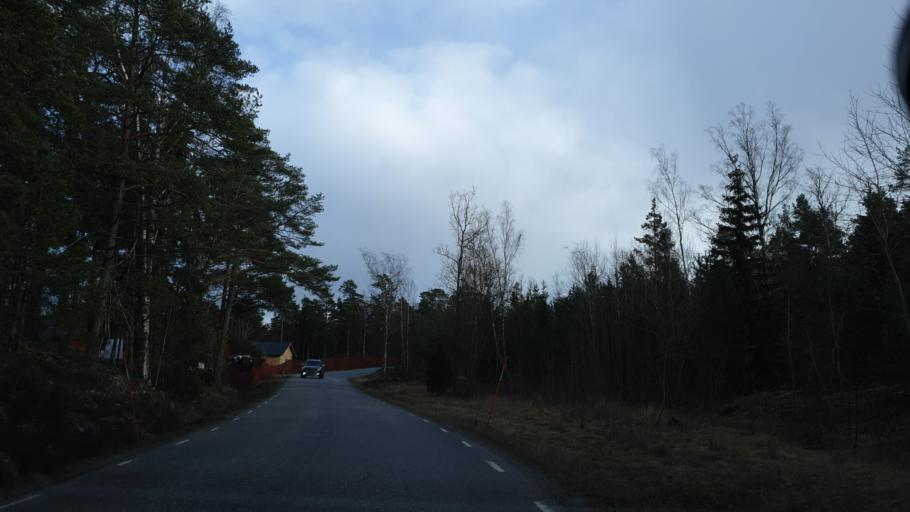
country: SE
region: Stockholm
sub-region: Varmdo Kommun
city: Holo
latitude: 59.3552
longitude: 18.7006
